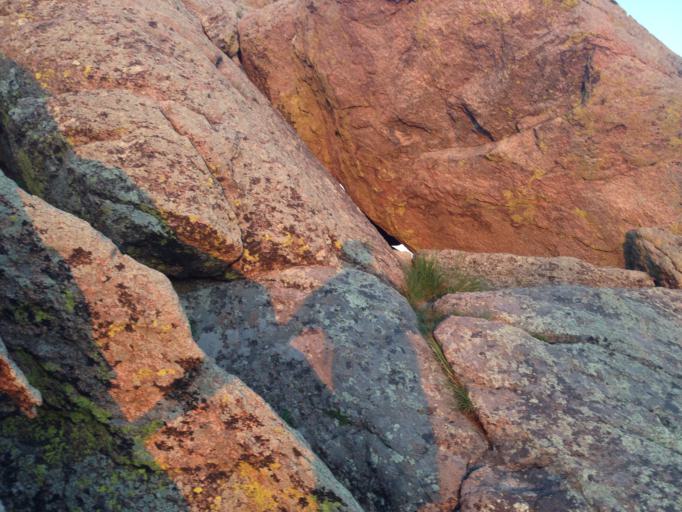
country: US
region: Colorado
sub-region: Larimer County
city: Laporte
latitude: 40.7178
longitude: -105.2895
